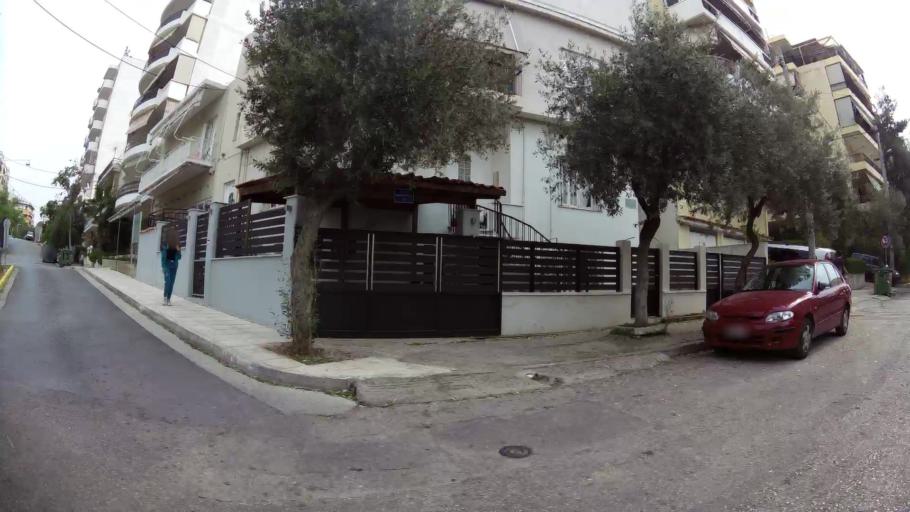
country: GR
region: Attica
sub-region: Nomarchia Athinas
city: Nea Ionia
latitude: 38.0309
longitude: 23.7517
